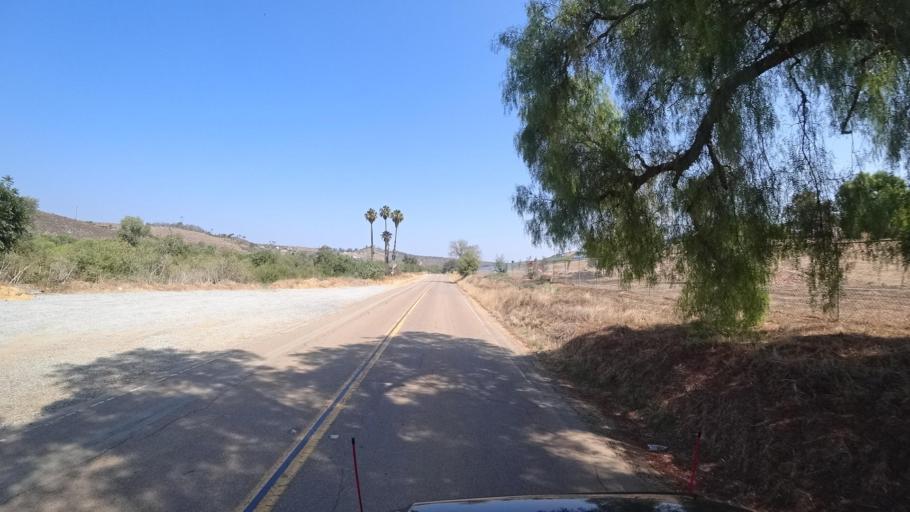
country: US
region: California
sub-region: San Diego County
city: Bonsall
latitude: 33.2677
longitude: -117.2331
